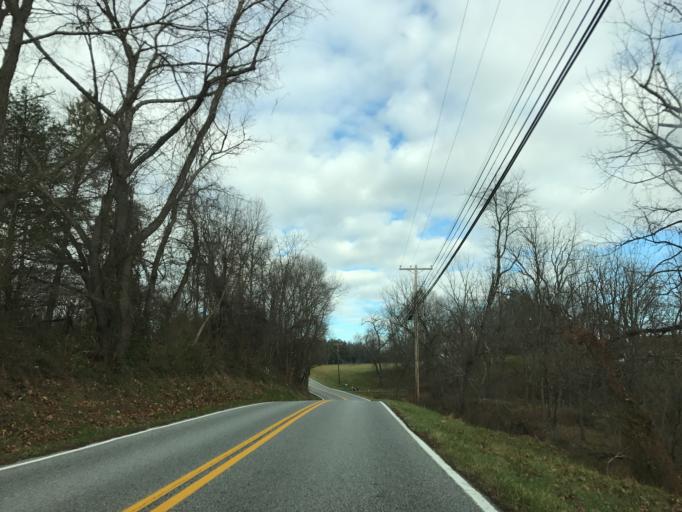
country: US
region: Pennsylvania
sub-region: York County
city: Stewartstown
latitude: 39.6409
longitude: -76.6273
